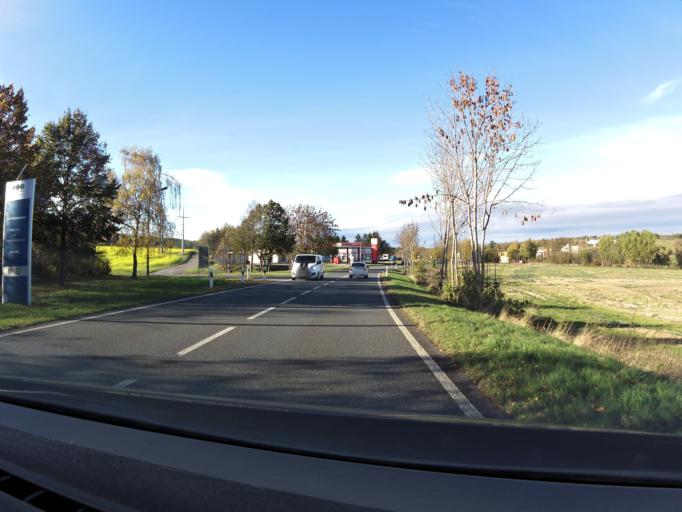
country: DE
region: Thuringia
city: Ilmenau
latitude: 50.6922
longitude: 10.9025
